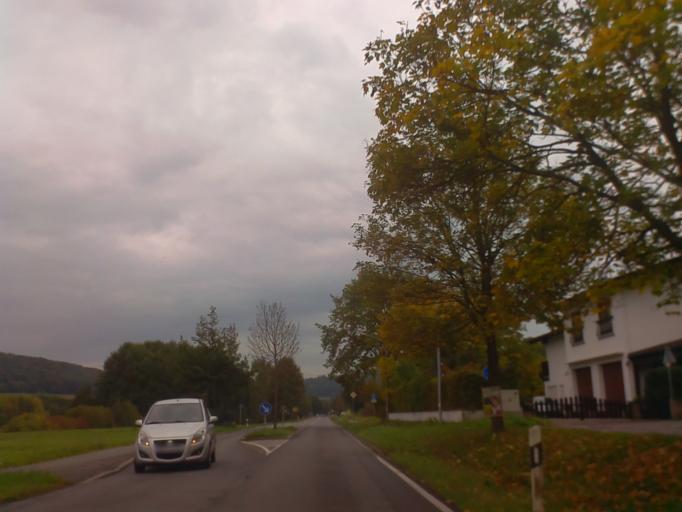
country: DE
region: Hesse
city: Hochst im Odenwald
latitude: 49.8274
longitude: 9.0423
